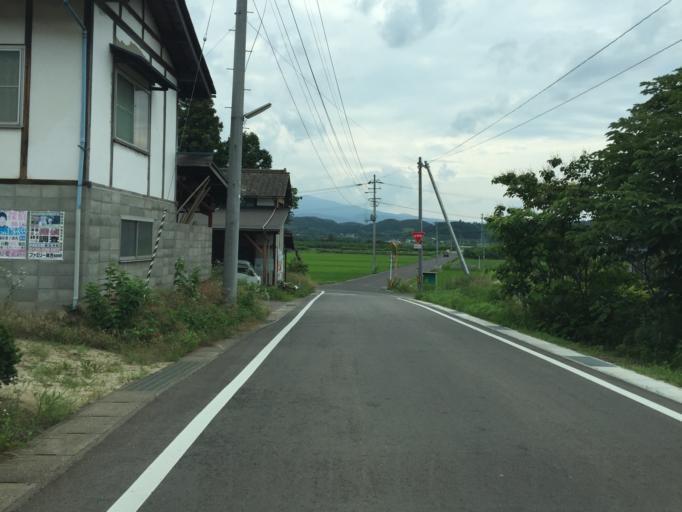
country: JP
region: Fukushima
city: Fukushima-shi
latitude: 37.7147
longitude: 140.4464
